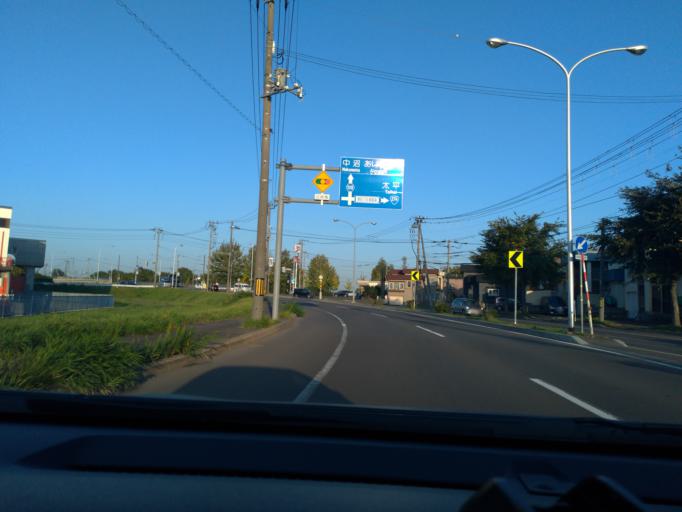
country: JP
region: Hokkaido
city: Ishikari
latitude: 43.1582
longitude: 141.3583
